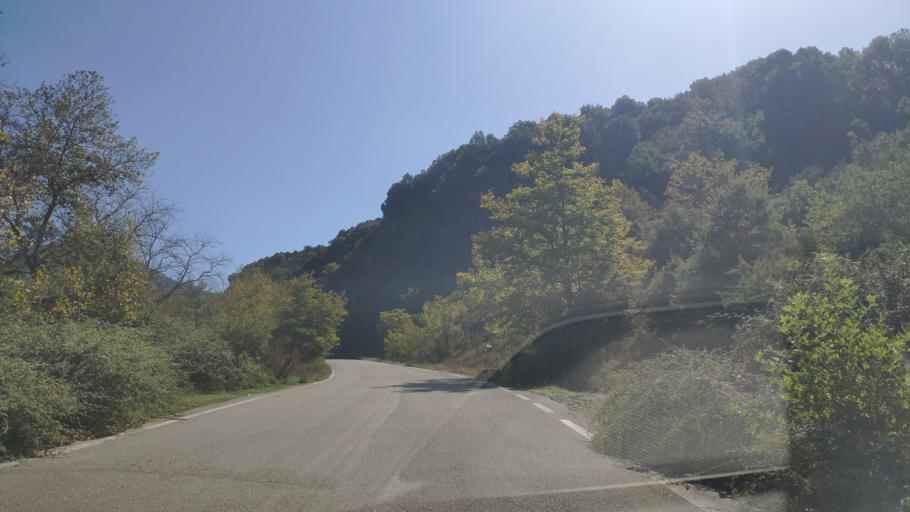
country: GR
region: West Greece
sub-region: Nomos Aitolias kai Akarnanias
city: Sardinia
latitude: 38.9240
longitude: 21.3794
